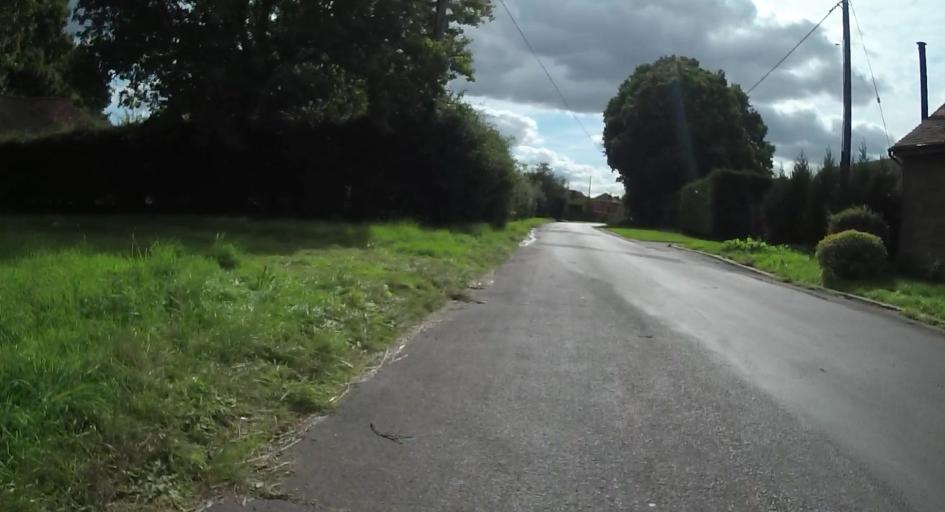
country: GB
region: England
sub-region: Surrey
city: Chobham
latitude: 51.3443
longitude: -0.6175
